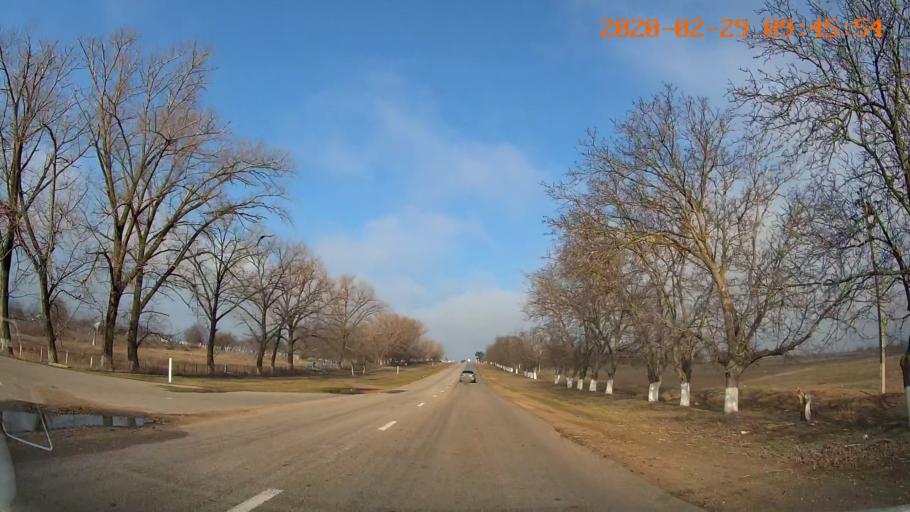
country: MD
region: Telenesti
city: Crasnoe
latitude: 46.6627
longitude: 29.8048
